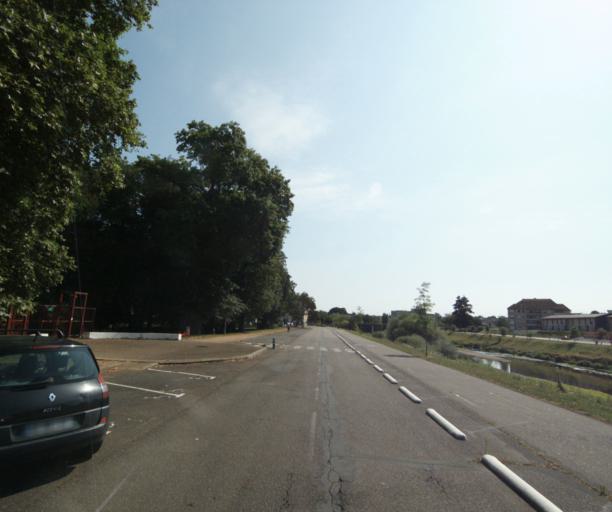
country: FR
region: Bourgogne
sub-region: Departement de Saone-et-Loire
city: Gueugnon
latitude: 46.5980
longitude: 4.0572
